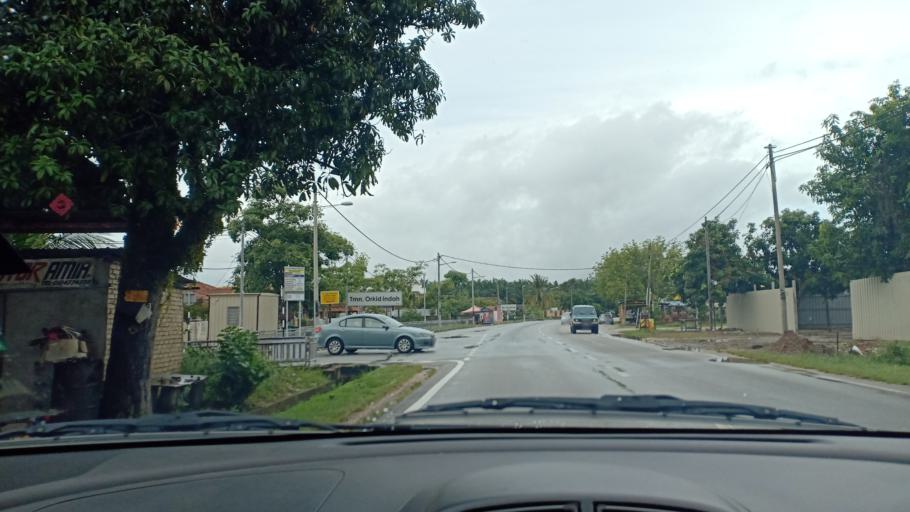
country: MY
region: Penang
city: Kepala Batas
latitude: 5.4946
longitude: 100.4484
